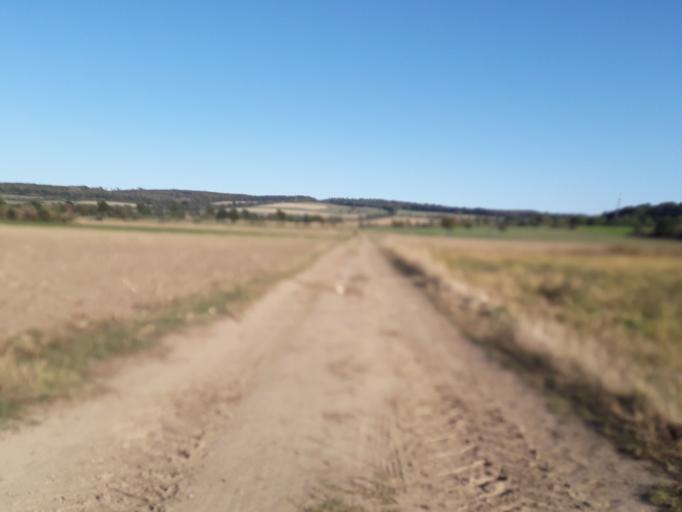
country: DE
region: North Rhine-Westphalia
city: Bad Lippspringe
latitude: 51.7626
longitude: 8.8302
